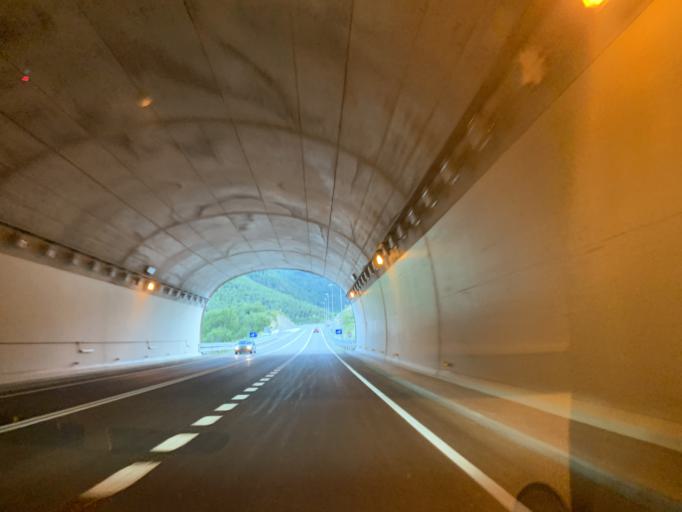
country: ES
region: Aragon
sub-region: Provincia de Huesca
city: Fiscal
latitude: 42.4942
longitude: -0.1526
